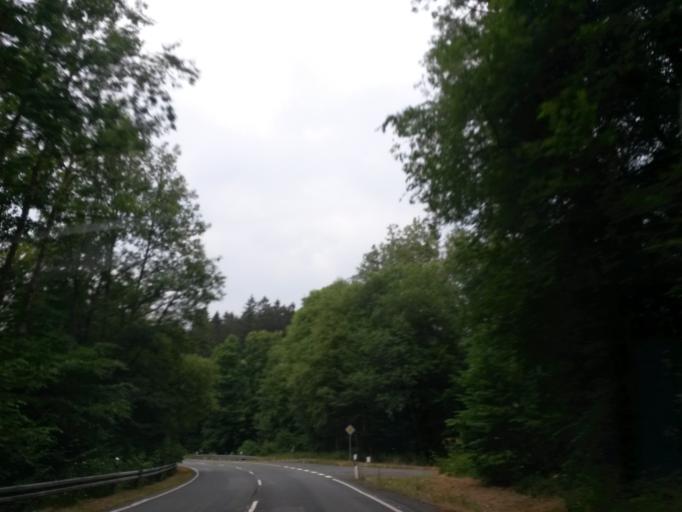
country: DE
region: North Rhine-Westphalia
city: Meinerzhagen
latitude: 51.0833
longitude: 7.6496
